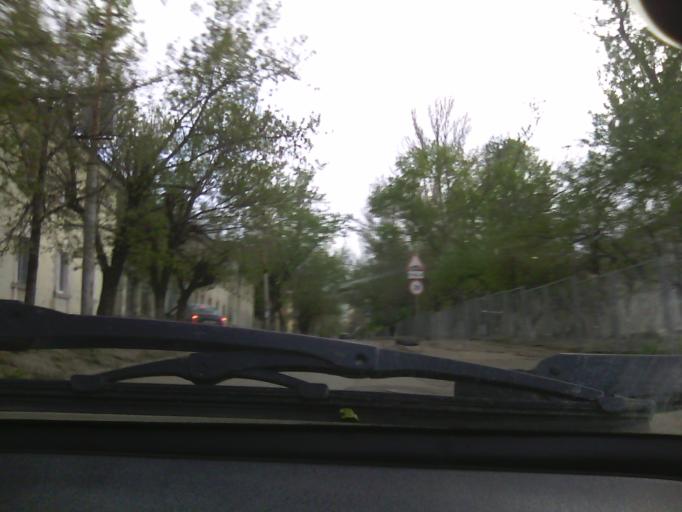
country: RU
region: Saratov
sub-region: Saratovskiy Rayon
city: Saratov
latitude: 51.5900
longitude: 45.9368
